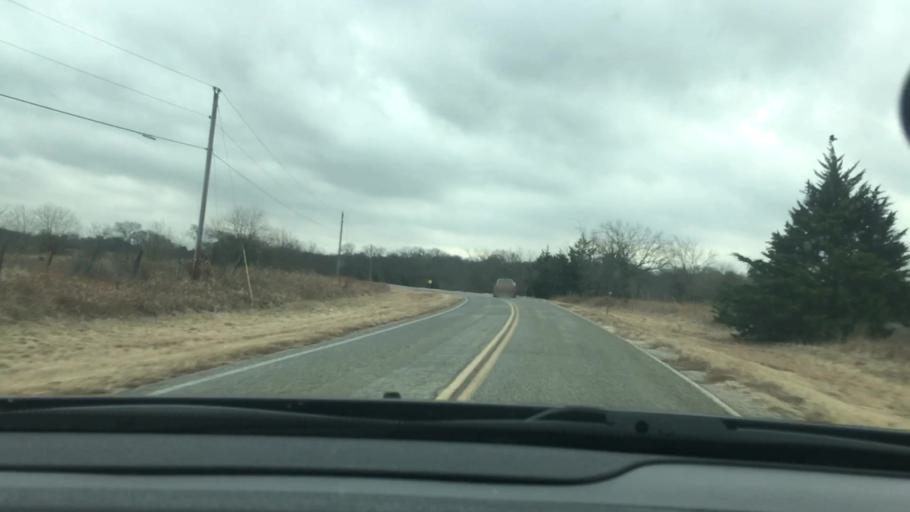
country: US
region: Oklahoma
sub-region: Johnston County
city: Tishomingo
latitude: 34.1442
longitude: -96.5482
